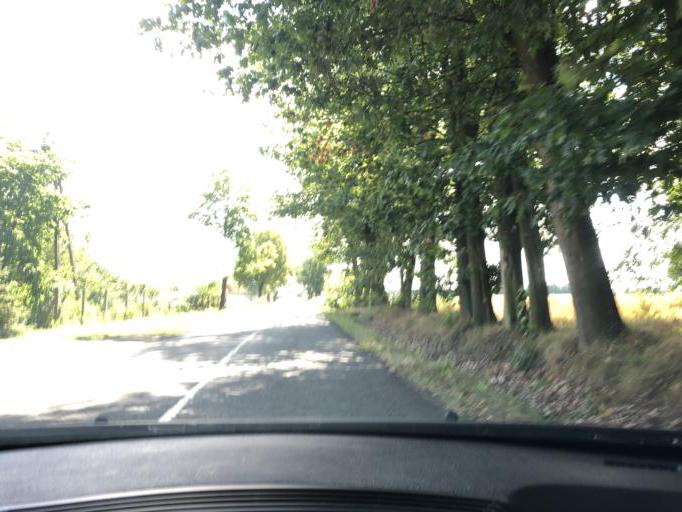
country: PL
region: Lodz Voivodeship
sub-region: Powiat wieruszowski
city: Czastary
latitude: 51.2396
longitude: 18.3370
